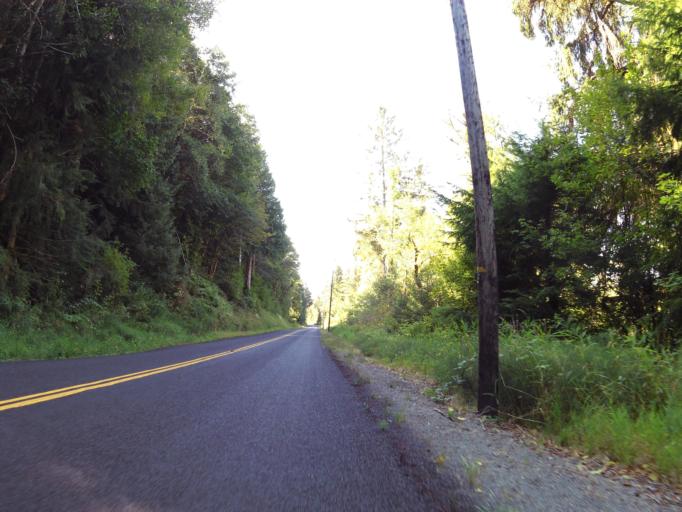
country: US
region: Washington
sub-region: Wahkiakum County
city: Cathlamet
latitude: 46.1929
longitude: -123.5738
